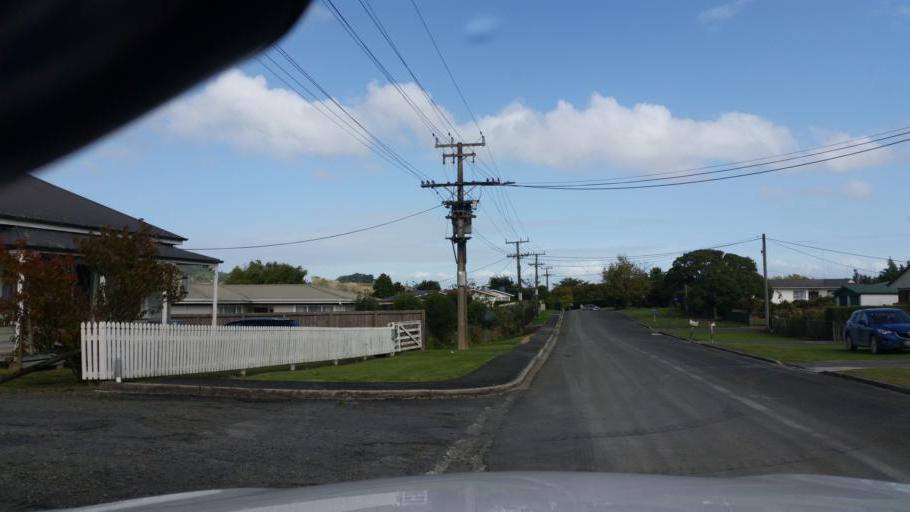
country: NZ
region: Northland
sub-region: Whangarei
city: Ruakaka
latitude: -36.1020
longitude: 174.3673
